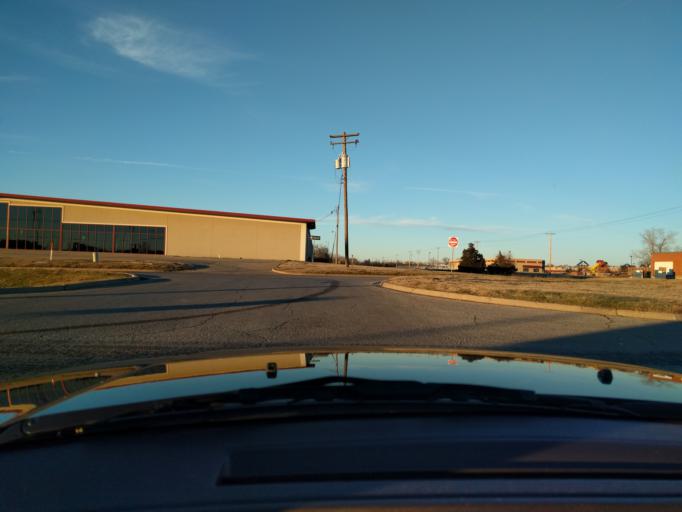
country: US
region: Oklahoma
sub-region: Oklahoma County
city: Warr Acres
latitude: 35.4641
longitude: -97.5966
